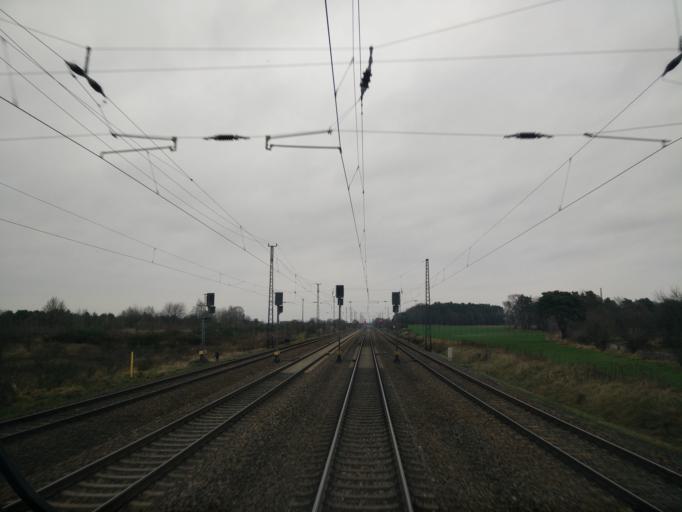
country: DE
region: Mecklenburg-Vorpommern
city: Sulstorf
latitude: 53.5583
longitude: 11.3670
